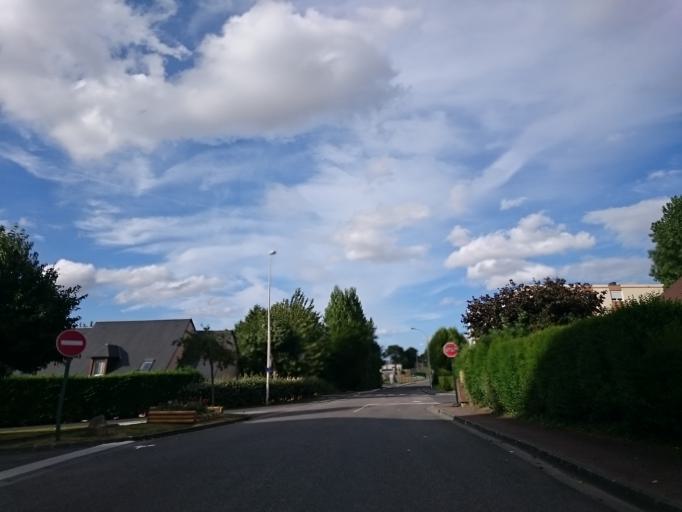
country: FR
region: Lower Normandy
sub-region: Departement du Calvados
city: Fleury-sur-Orne
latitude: 49.1433
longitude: -0.3831
